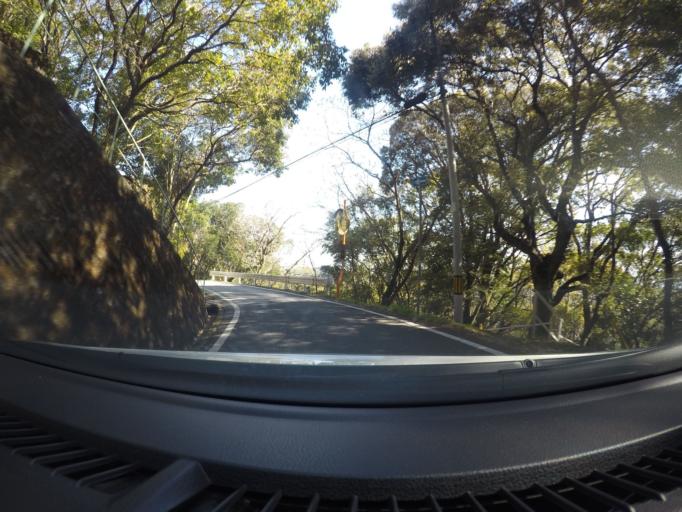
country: JP
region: Kochi
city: Kochi-shi
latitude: 33.5454
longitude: 133.5754
